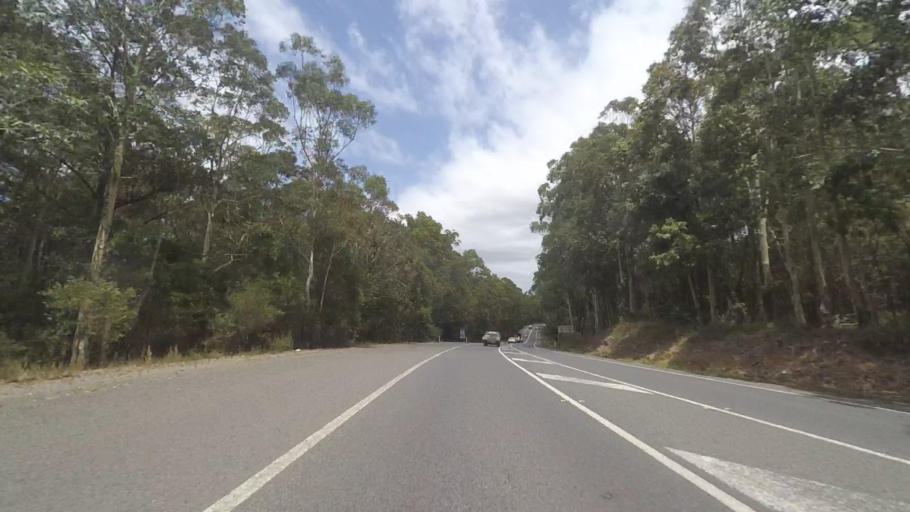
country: AU
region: New South Wales
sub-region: Shoalhaven Shire
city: Falls Creek
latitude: -35.0838
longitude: 150.5427
